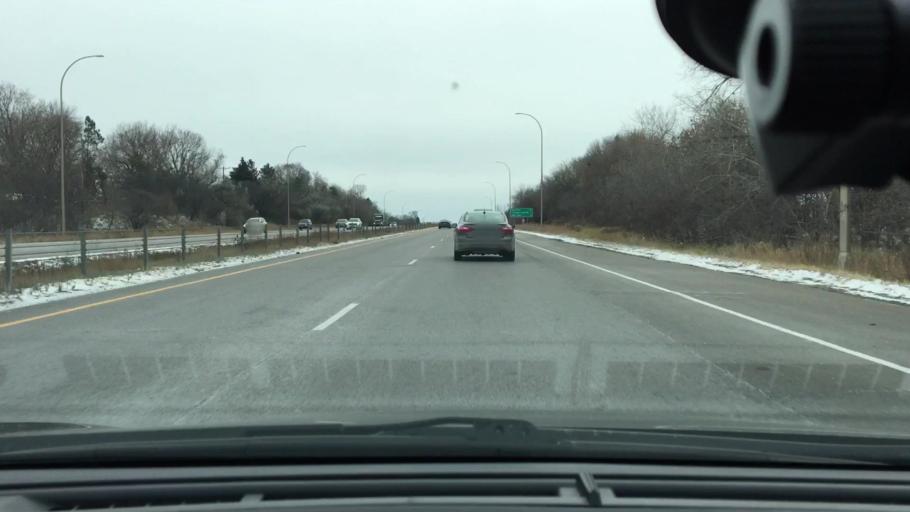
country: US
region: Minnesota
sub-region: Hennepin County
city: Osseo
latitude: 45.0774
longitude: -93.4020
